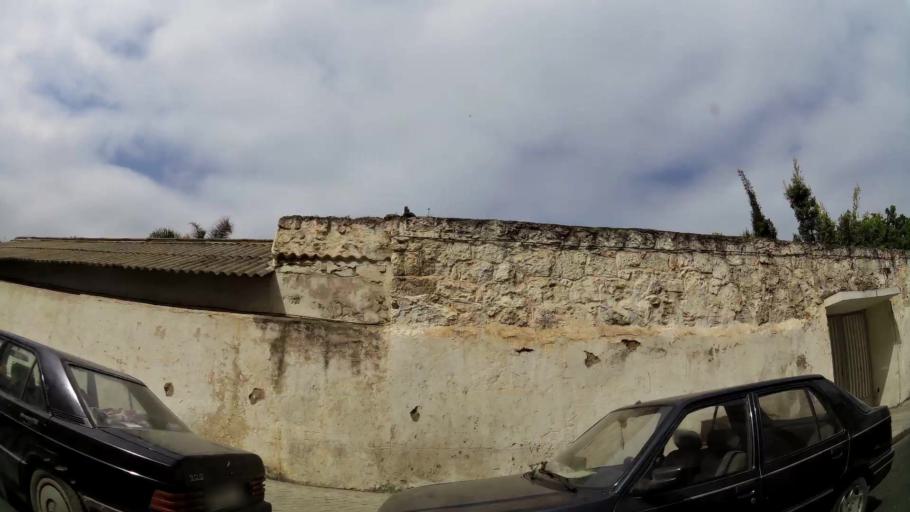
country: MA
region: Rabat-Sale-Zemmour-Zaer
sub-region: Rabat
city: Rabat
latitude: 34.0186
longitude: -6.8518
